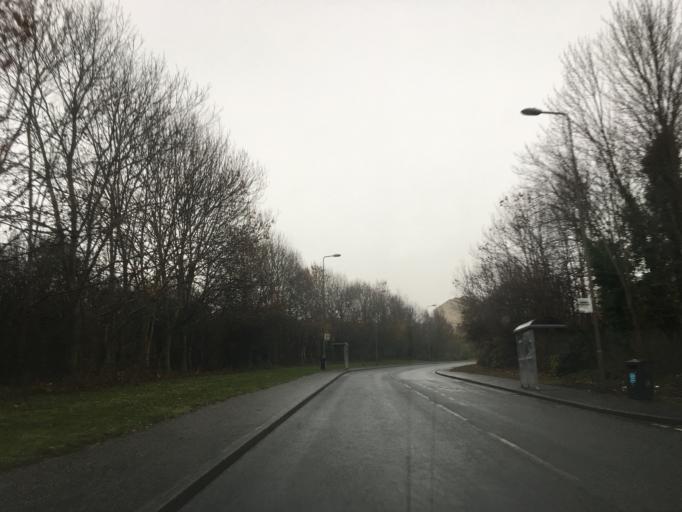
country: GB
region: Scotland
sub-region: Edinburgh
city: Colinton
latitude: 55.9146
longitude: -3.2770
